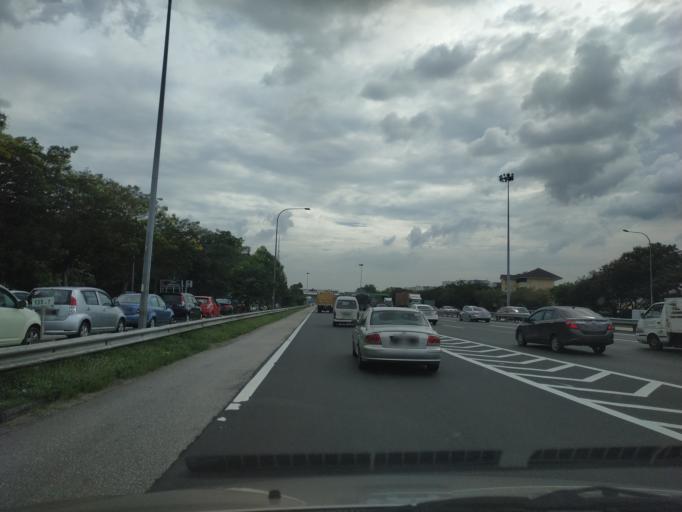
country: MY
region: Penang
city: Perai
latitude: 5.3957
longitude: 100.4063
